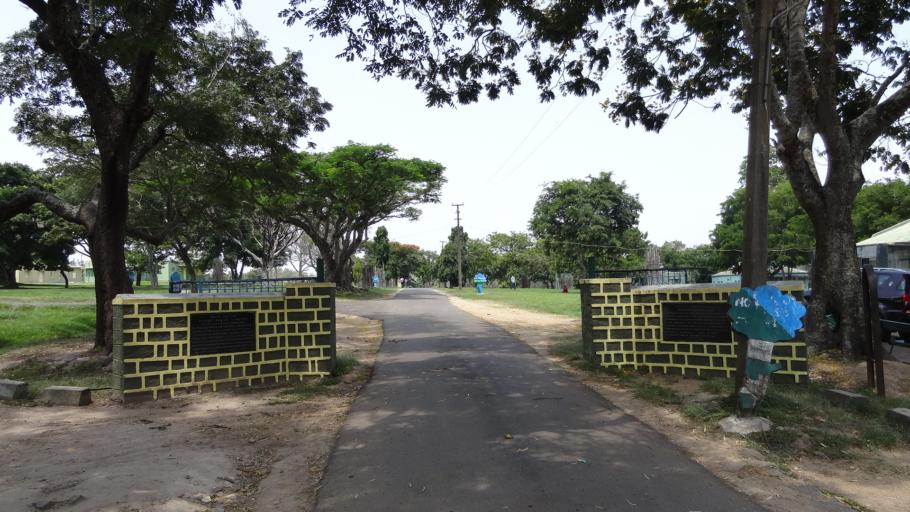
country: IN
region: Tamil Nadu
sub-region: Nilgiri
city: Masinigudi
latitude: 11.6676
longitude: 76.6287
